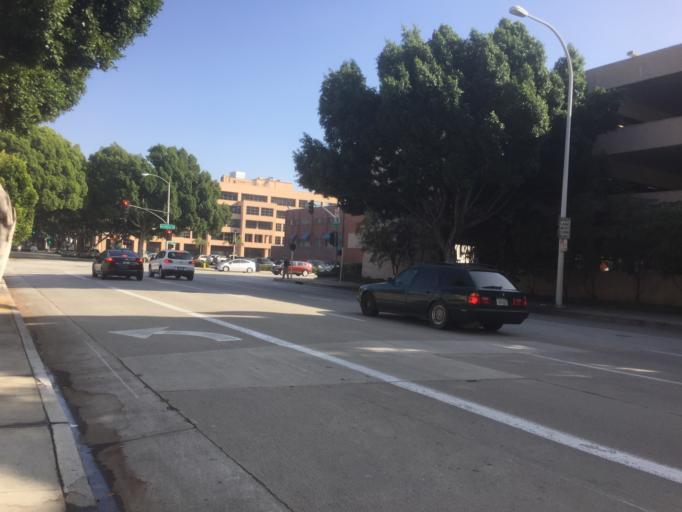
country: US
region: California
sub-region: Los Angeles County
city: Pasadena
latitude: 34.1447
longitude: -118.1421
